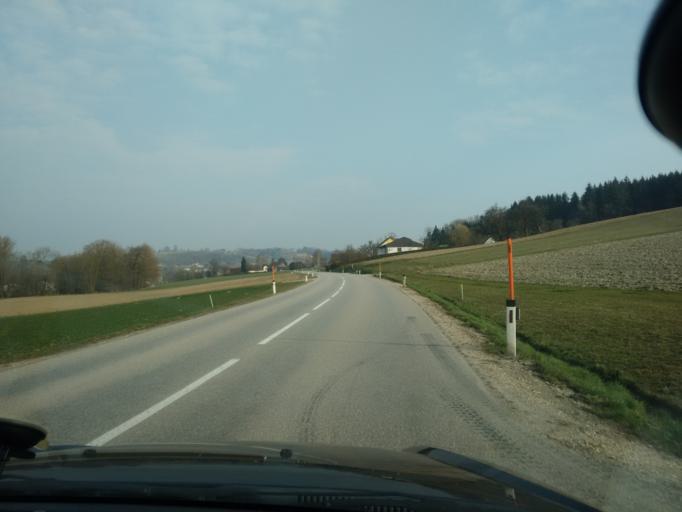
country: AT
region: Upper Austria
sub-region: Politischer Bezirk Grieskirchen
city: Bad Schallerbach
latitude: 48.2529
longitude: 13.9614
